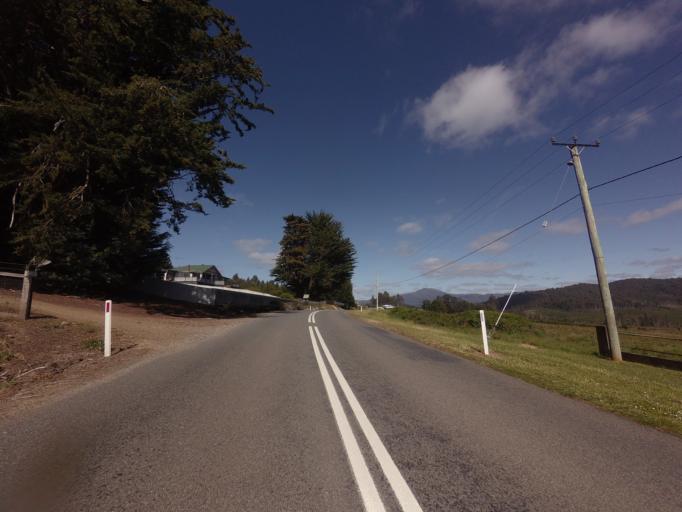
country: AU
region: Tasmania
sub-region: Derwent Valley
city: New Norfolk
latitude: -42.7490
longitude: 146.6469
